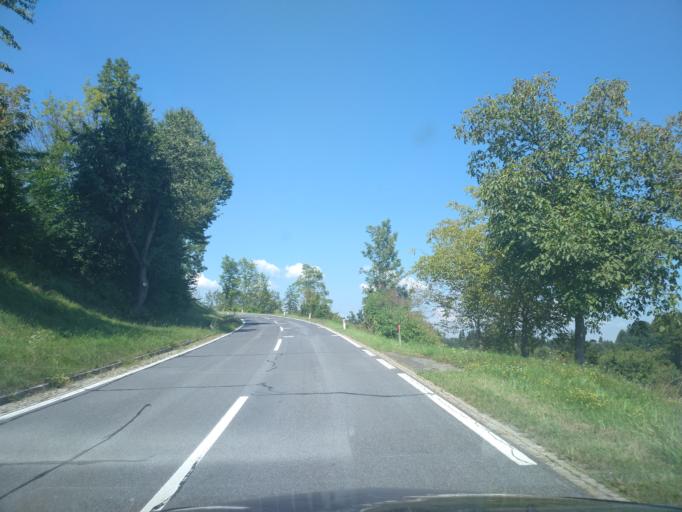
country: AT
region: Styria
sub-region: Politischer Bezirk Leibnitz
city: Leutschach
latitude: 46.6768
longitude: 15.4798
